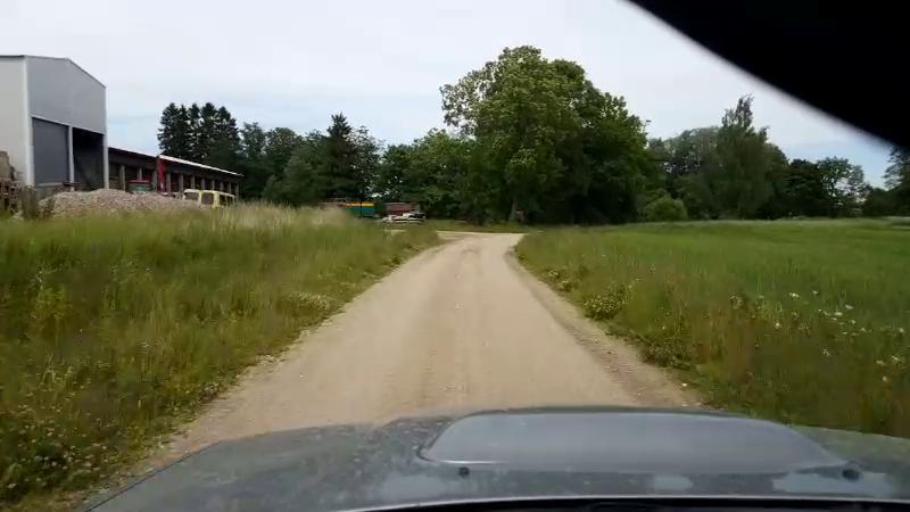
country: EE
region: Paernumaa
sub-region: Tootsi vald
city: Tootsi
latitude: 58.5372
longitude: 24.7337
